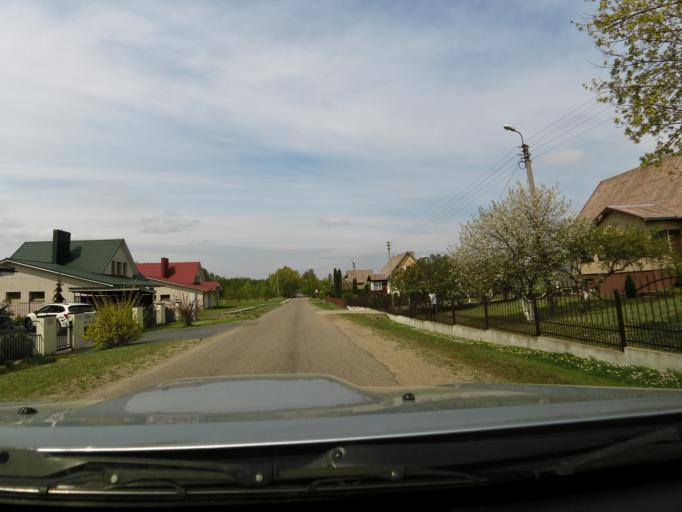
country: LT
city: Salcininkai
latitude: 54.4291
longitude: 25.3118
